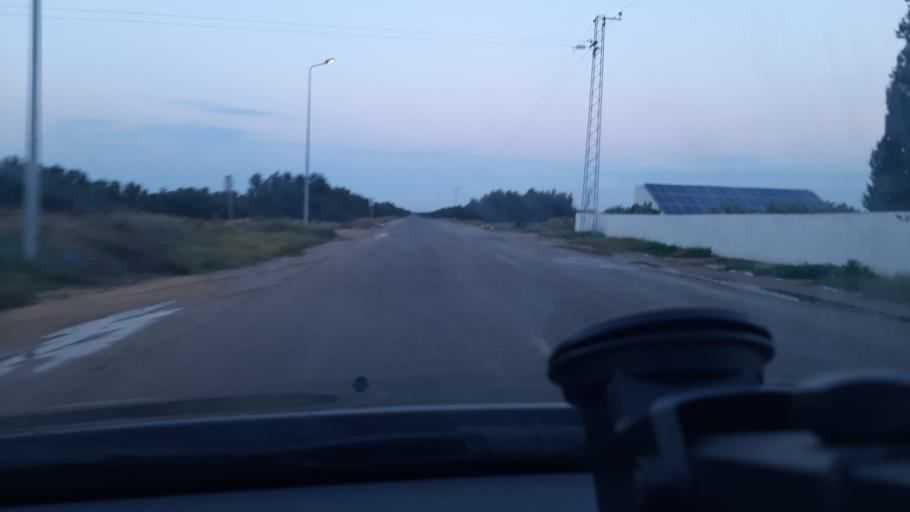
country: TN
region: Al Mahdiyah
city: Shurban
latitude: 35.0235
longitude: 10.4708
